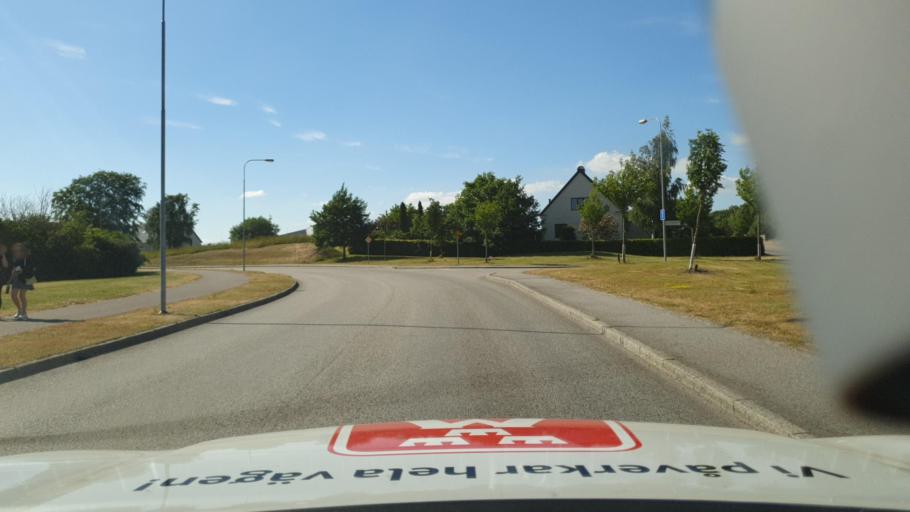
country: SE
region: Skane
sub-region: Skurups Kommun
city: Skurup
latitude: 55.4888
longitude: 13.4926
